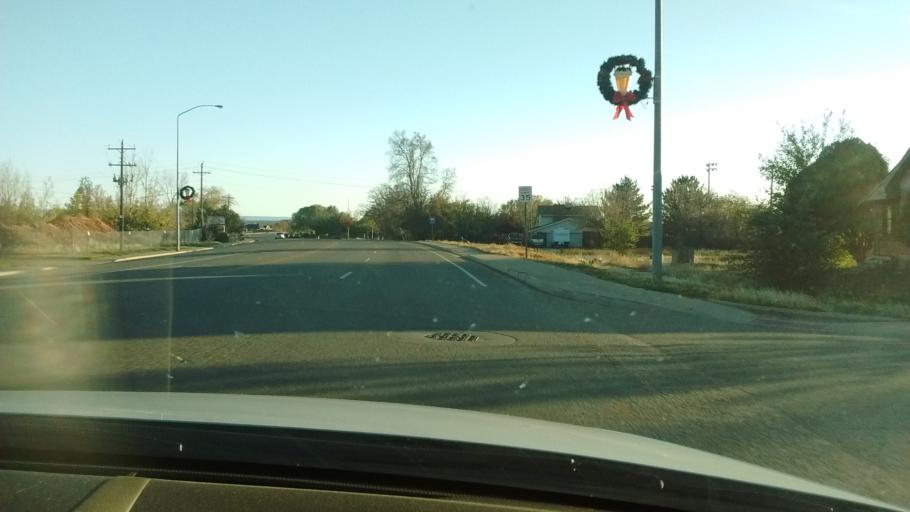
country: US
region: Utah
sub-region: Kane County
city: Kanab
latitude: 37.0413
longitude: -112.5265
